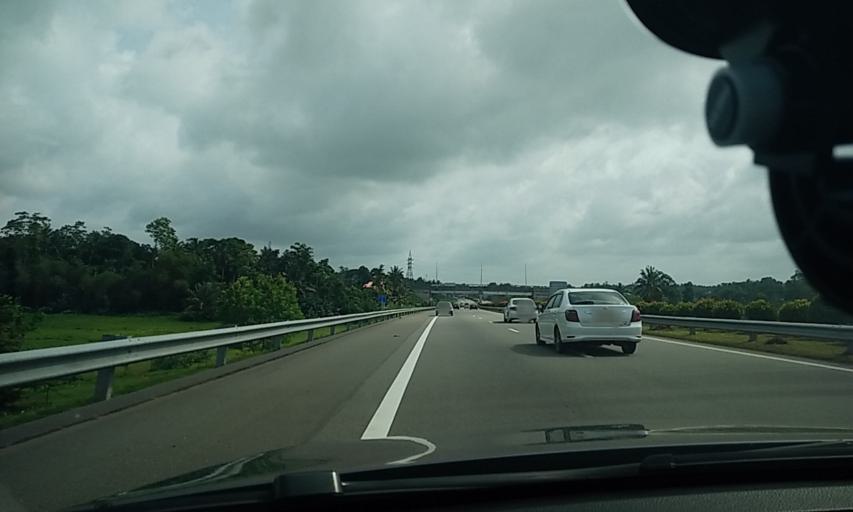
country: LK
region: Western
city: Homagama
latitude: 6.8463
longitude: 79.9790
